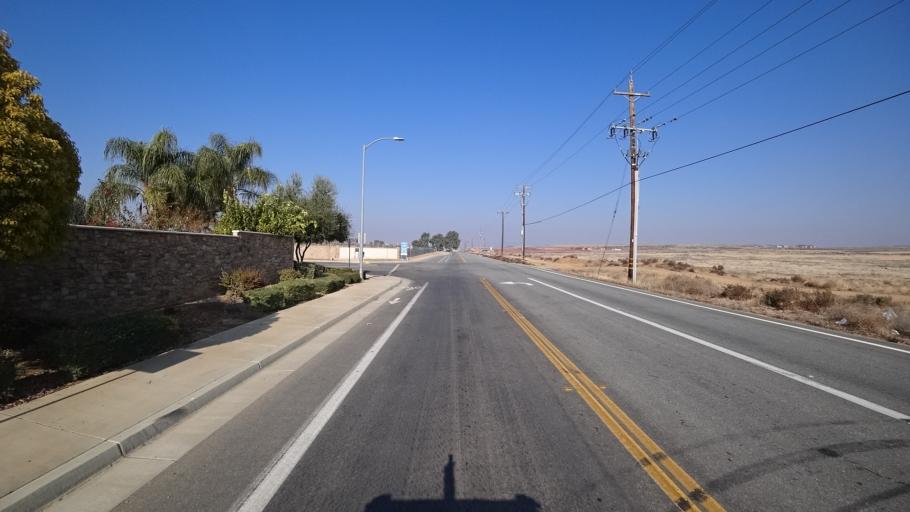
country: US
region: California
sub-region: Kern County
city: Oildale
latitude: 35.4095
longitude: -118.8788
